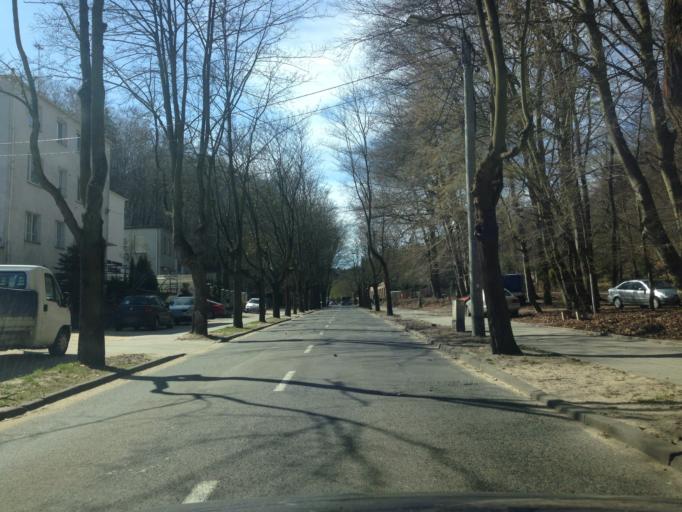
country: PL
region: Pomeranian Voivodeship
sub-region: Gdynia
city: Gdynia
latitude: 54.5107
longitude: 18.5241
